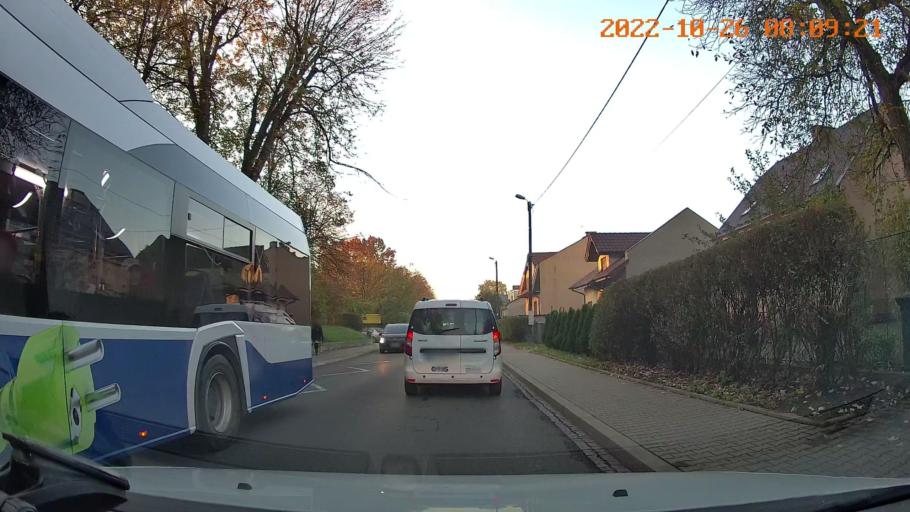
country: PL
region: Lesser Poland Voivodeship
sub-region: Krakow
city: Krakow
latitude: 50.0850
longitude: 19.9163
